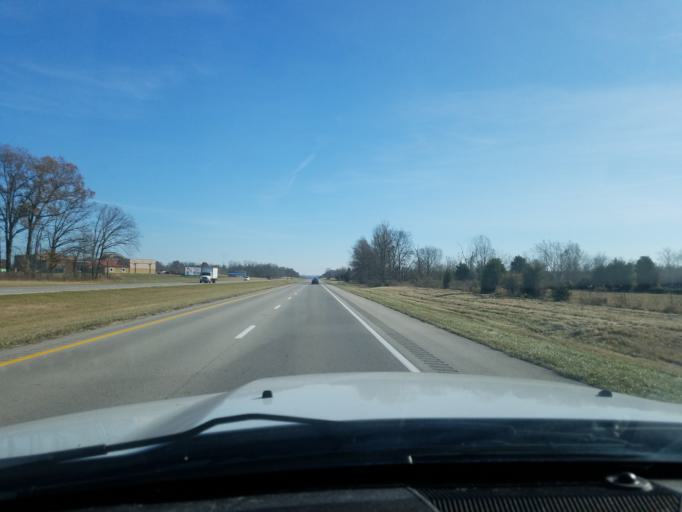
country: US
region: Ohio
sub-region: Adams County
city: Winchester
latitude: 38.9327
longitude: -83.5889
